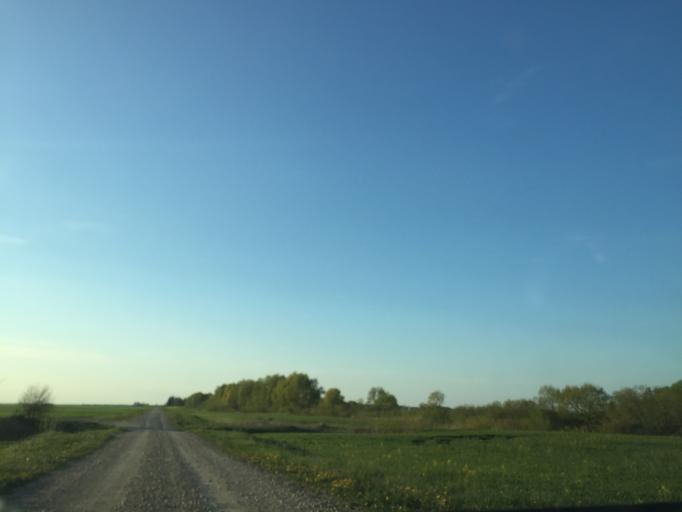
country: LV
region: Bauskas Rajons
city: Bauska
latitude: 56.2942
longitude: 24.1815
